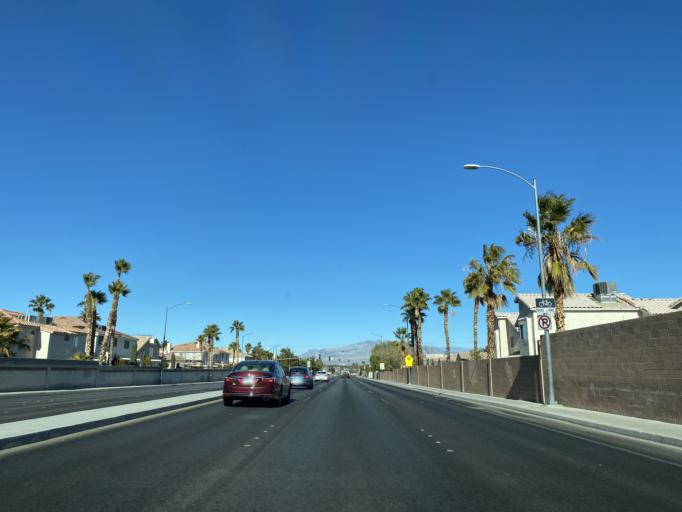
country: US
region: Nevada
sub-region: Clark County
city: Summerlin South
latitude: 36.2287
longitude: -115.2790
